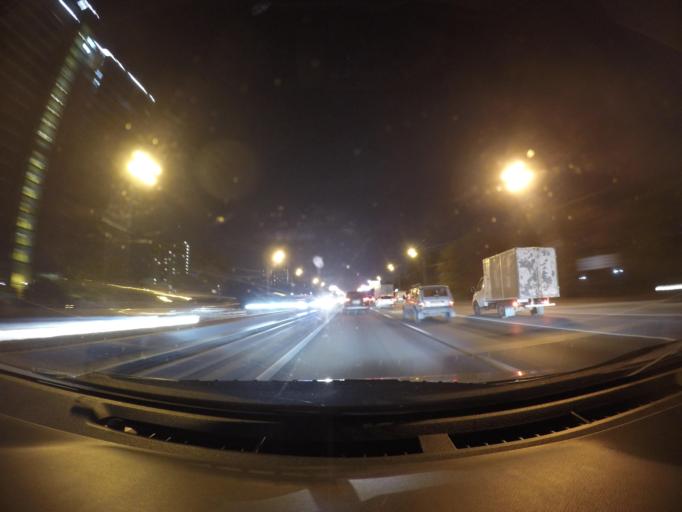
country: RU
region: Moscow
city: Khimki
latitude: 55.8952
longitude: 37.4290
